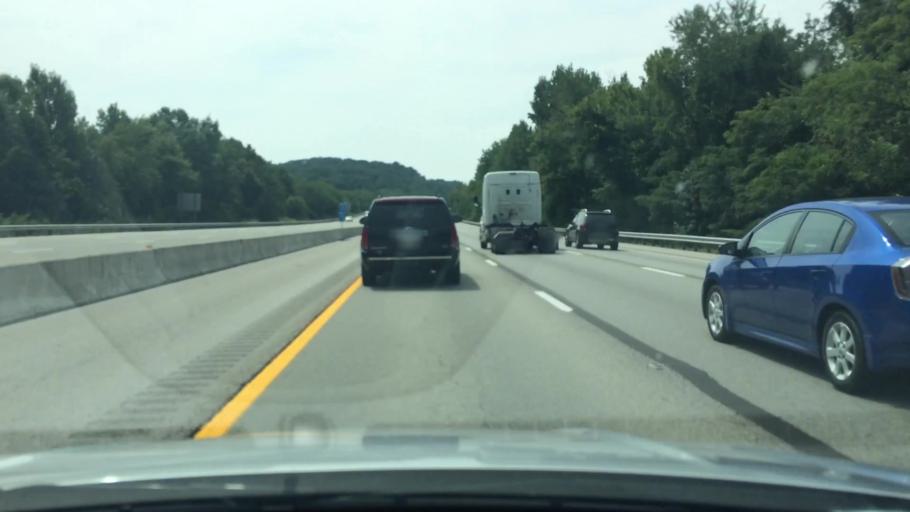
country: US
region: Kentucky
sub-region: Madison County
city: Berea
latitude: 37.5534
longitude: -84.3166
